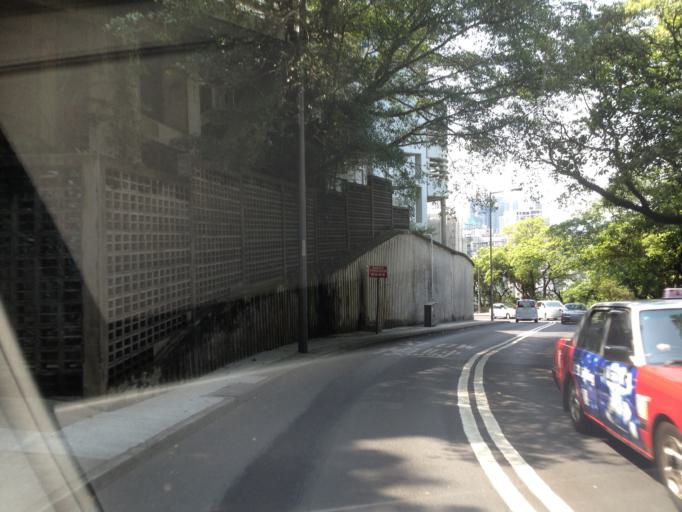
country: HK
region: Central and Western
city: Central
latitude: 22.2732
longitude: 114.1597
